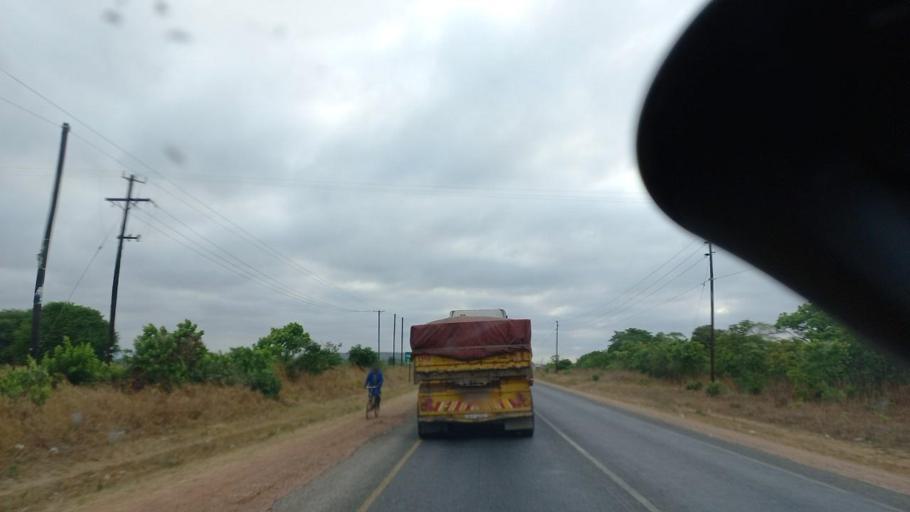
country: ZM
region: Lusaka
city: Chongwe
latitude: -15.3489
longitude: 28.5705
